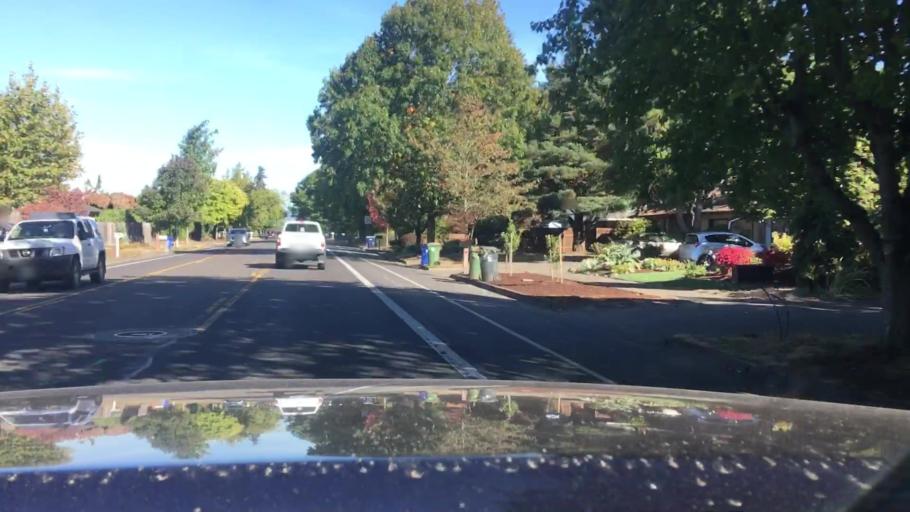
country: US
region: Oregon
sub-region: Lane County
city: Eugene
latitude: 44.0696
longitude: -123.0633
